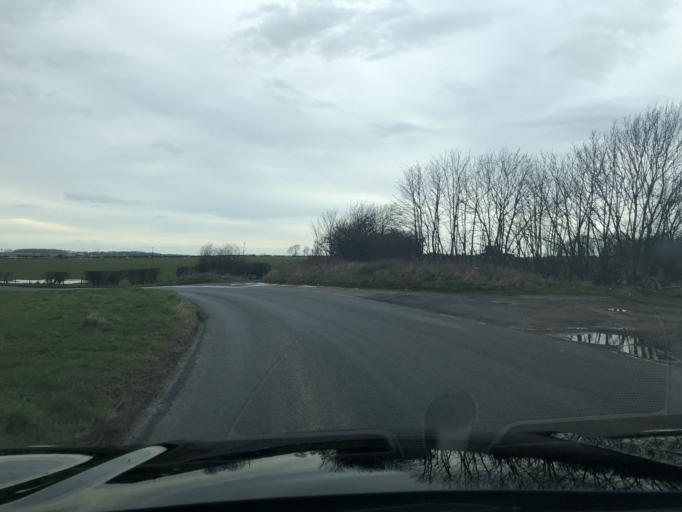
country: GB
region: England
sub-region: North Yorkshire
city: Northallerton
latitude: 54.3416
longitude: -1.4535
